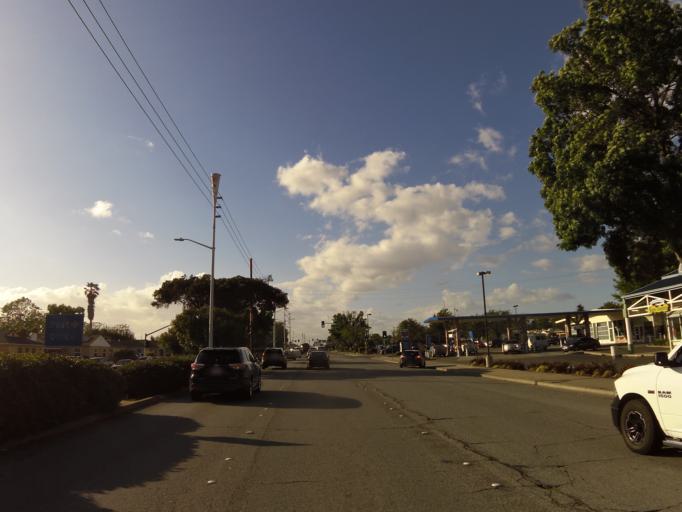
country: US
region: California
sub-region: Alameda County
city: San Lorenzo
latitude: 37.6806
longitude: -122.1275
